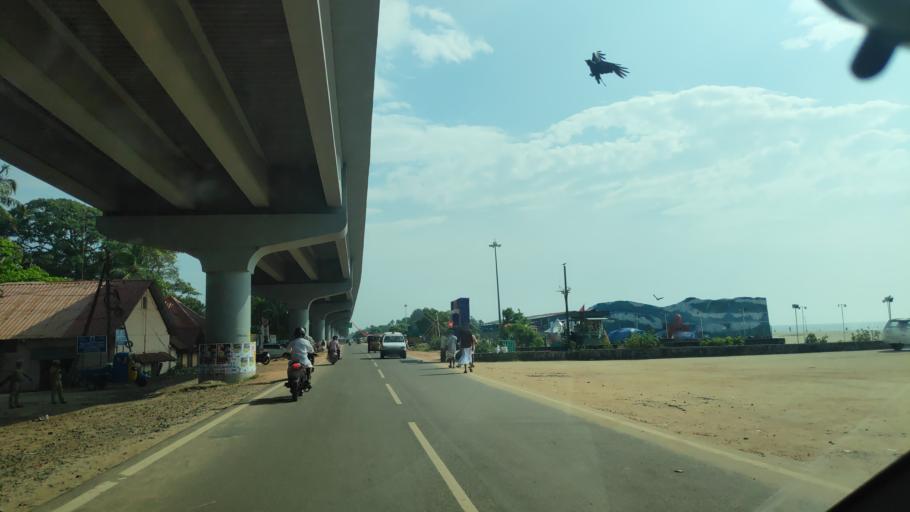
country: IN
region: Kerala
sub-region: Alappuzha
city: Alleppey
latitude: 9.4906
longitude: 76.3192
